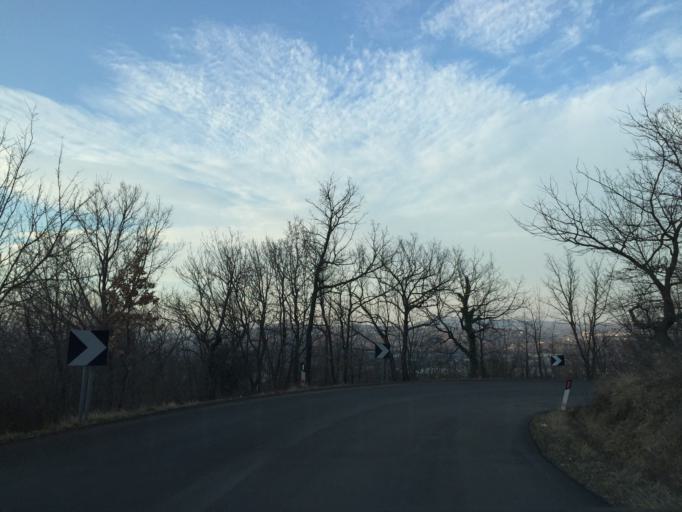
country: IT
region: Molise
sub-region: Provincia di Campobasso
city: Guardiaregia
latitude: 41.4475
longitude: 14.5522
